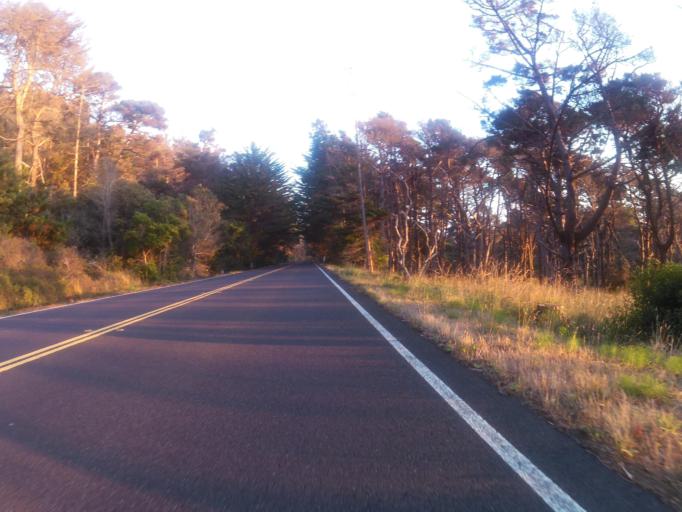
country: US
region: California
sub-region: Sonoma County
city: Sea Ranch
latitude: 38.6126
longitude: -123.3648
